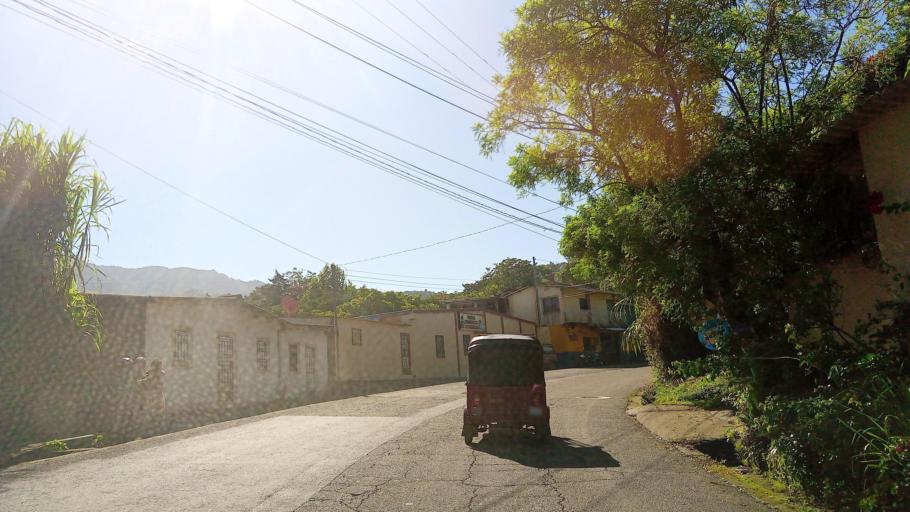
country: HN
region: Ocotepeque
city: Antigua Ocotepeque
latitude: 14.3137
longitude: -89.1636
